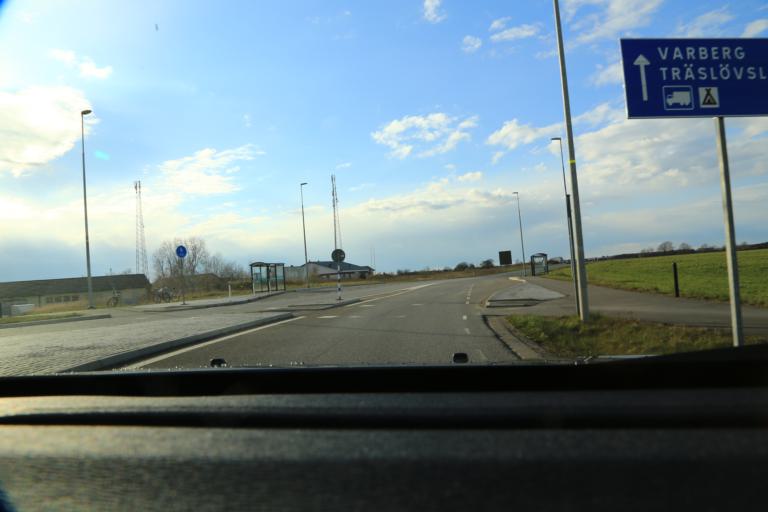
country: SE
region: Halland
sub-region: Varbergs Kommun
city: Traslovslage
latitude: 57.0566
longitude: 12.2992
